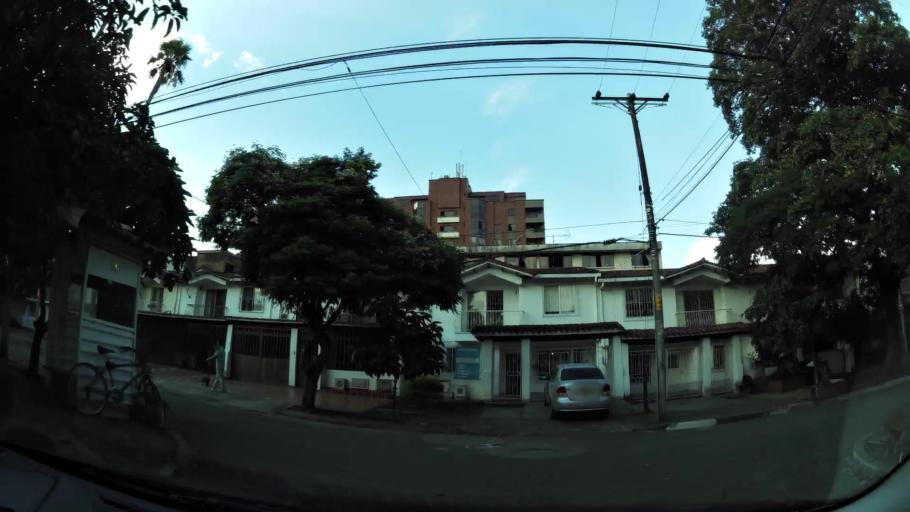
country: CO
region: Valle del Cauca
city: Cali
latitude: 3.4069
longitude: -76.5549
